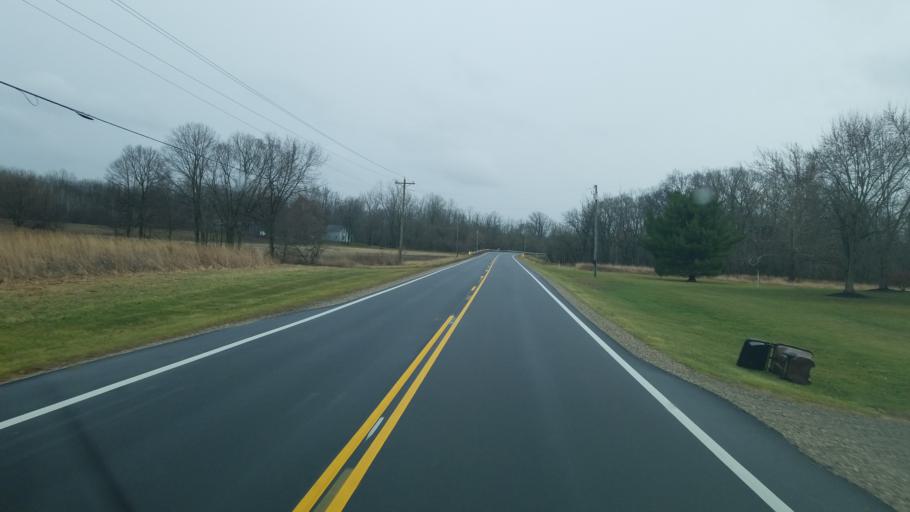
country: US
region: Ohio
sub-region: Union County
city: Richwood
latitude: 40.3860
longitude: -83.4067
